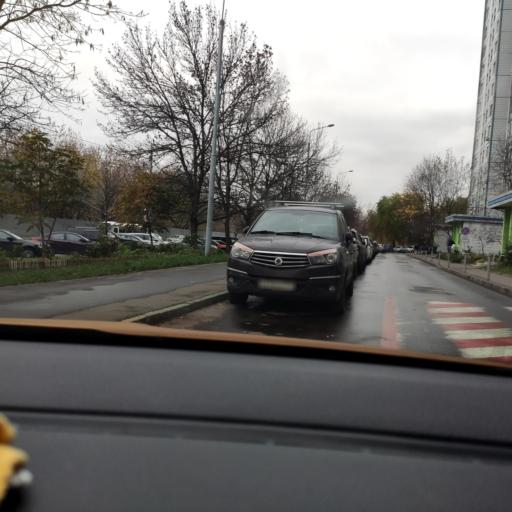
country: RU
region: Moscow
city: Zyablikovo
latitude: 55.6112
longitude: 37.7573
